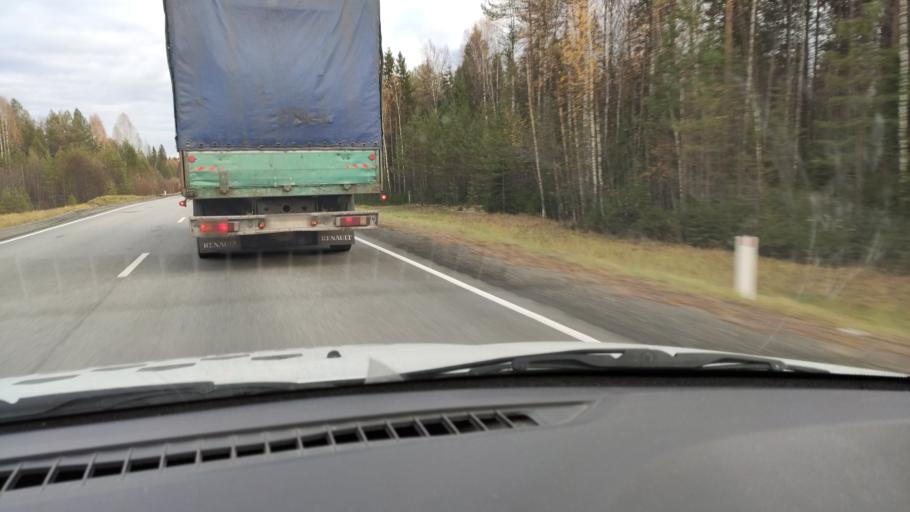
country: RU
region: Kirov
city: Dubrovka
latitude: 58.9065
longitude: 51.2592
